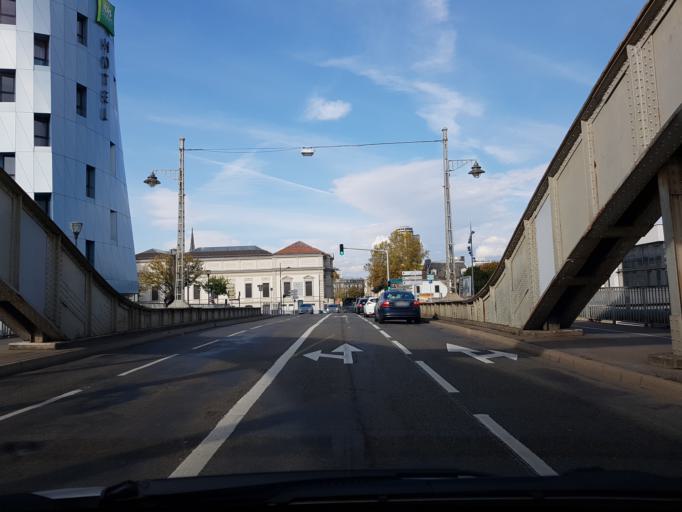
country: FR
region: Alsace
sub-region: Departement du Haut-Rhin
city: Mulhouse
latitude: 47.7439
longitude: 7.3465
